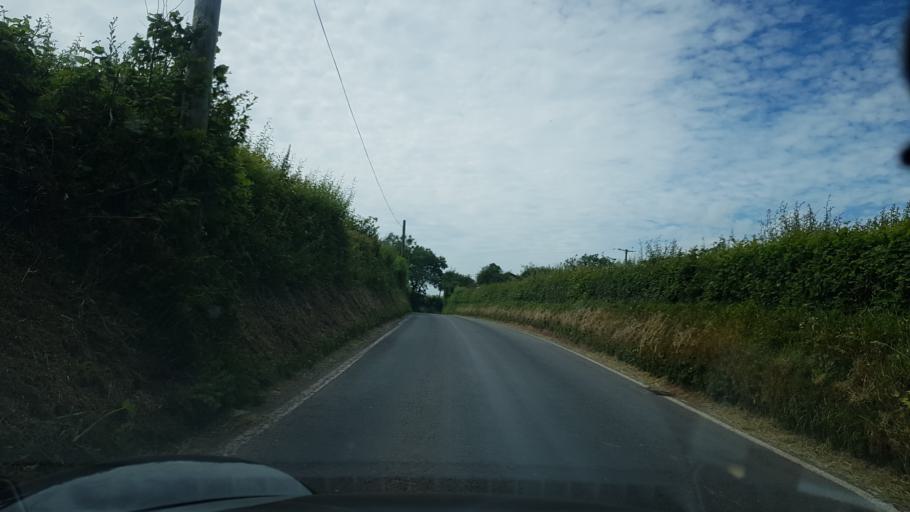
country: GB
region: Wales
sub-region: Carmarthenshire
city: Llanddowror
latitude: 51.7644
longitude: -4.5729
